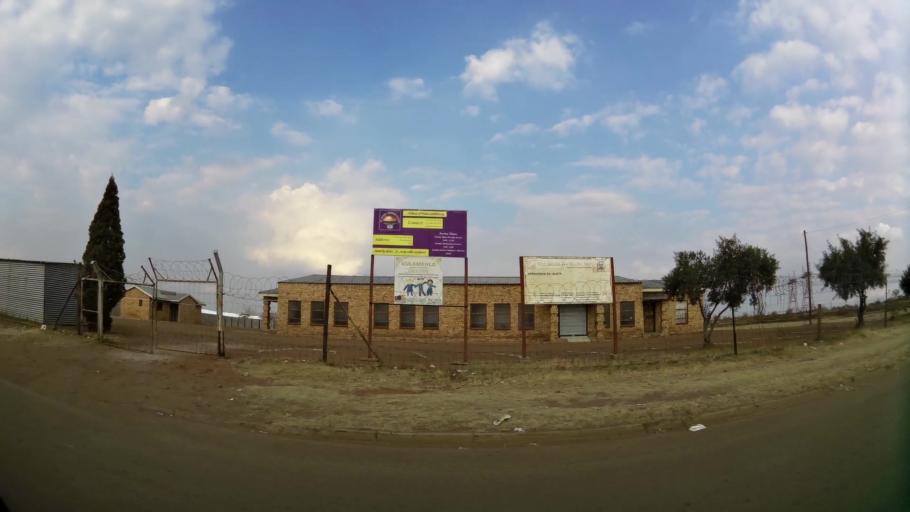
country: ZA
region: Gauteng
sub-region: Sedibeng District Municipality
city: Vanderbijlpark
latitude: -26.6949
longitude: 27.8776
